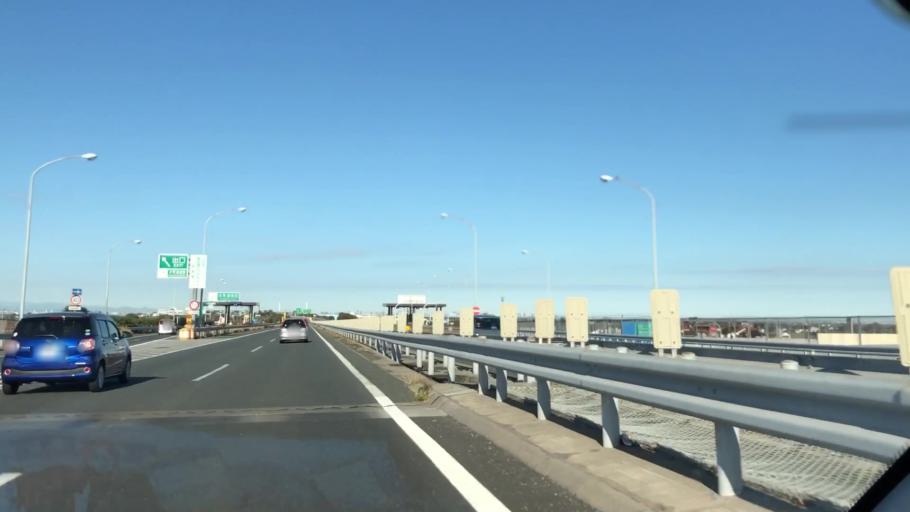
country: JP
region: Chiba
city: Kisarazu
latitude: 35.4269
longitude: 139.9297
